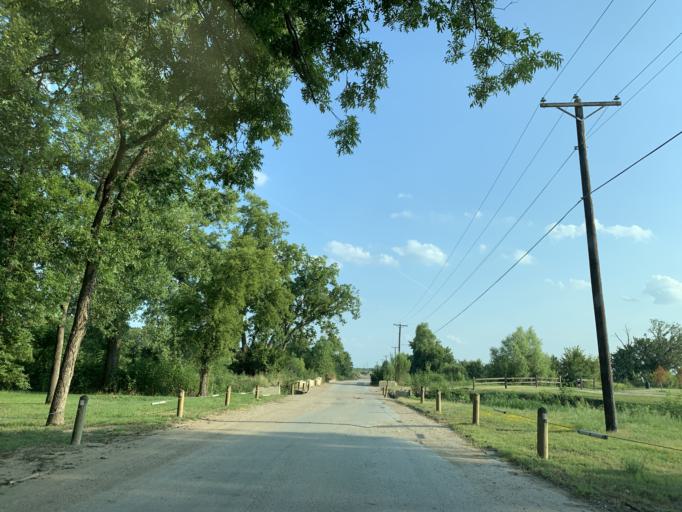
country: US
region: Texas
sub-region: Tarrant County
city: Hurst
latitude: 32.7988
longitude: -97.1692
